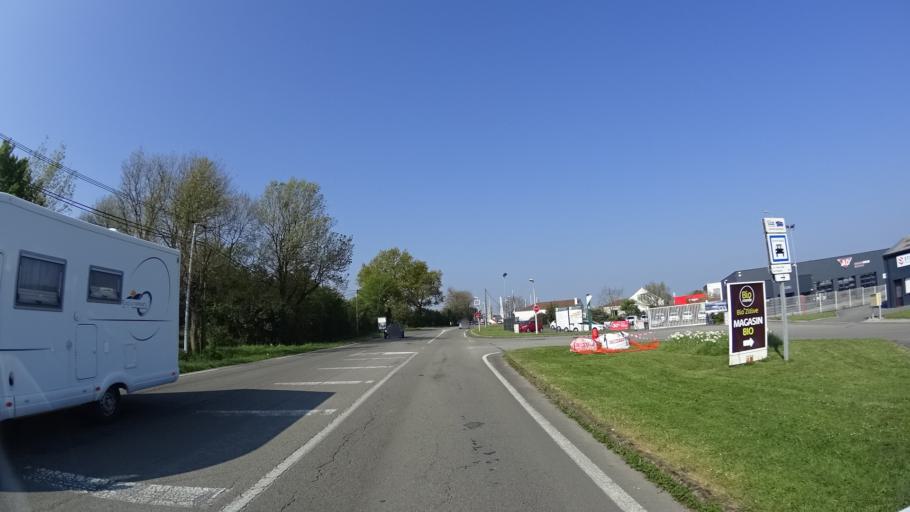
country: FR
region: Pays de la Loire
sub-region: Departement de la Loire-Atlantique
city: Sainte-Pazanne
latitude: 47.1032
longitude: -1.7996
